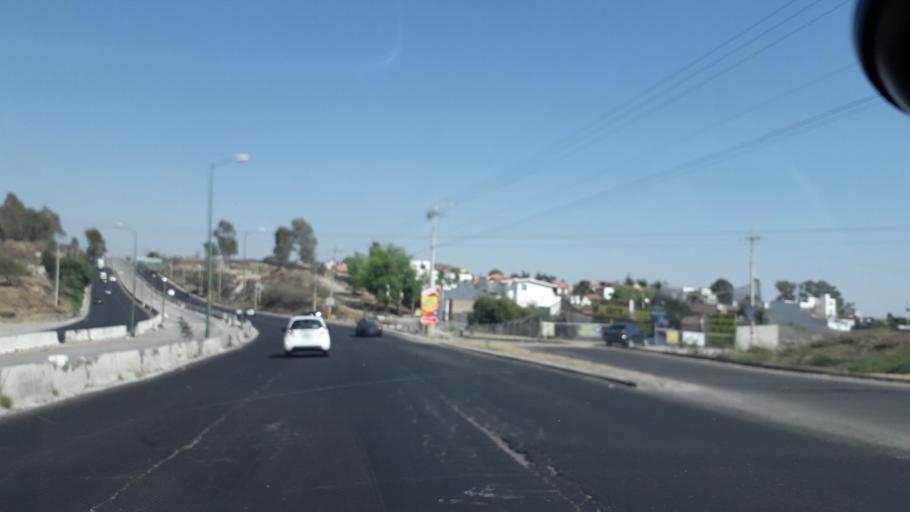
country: MX
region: Puebla
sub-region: Puebla
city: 18 de Marzo
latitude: 18.9732
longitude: -98.2092
